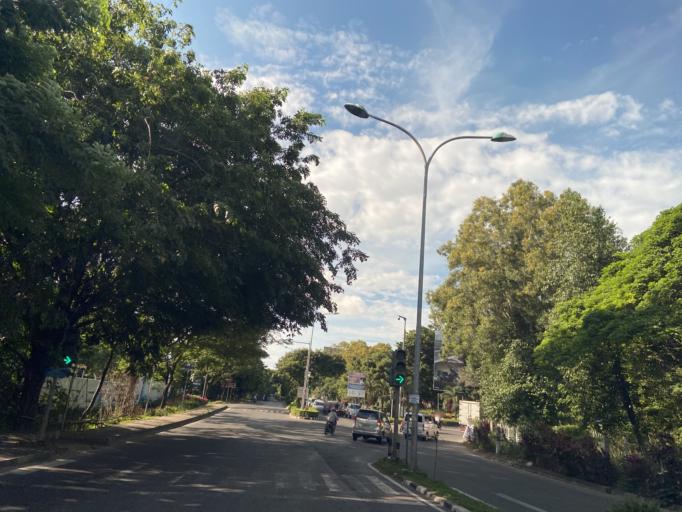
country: SG
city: Singapore
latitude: 1.1198
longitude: 104.0042
